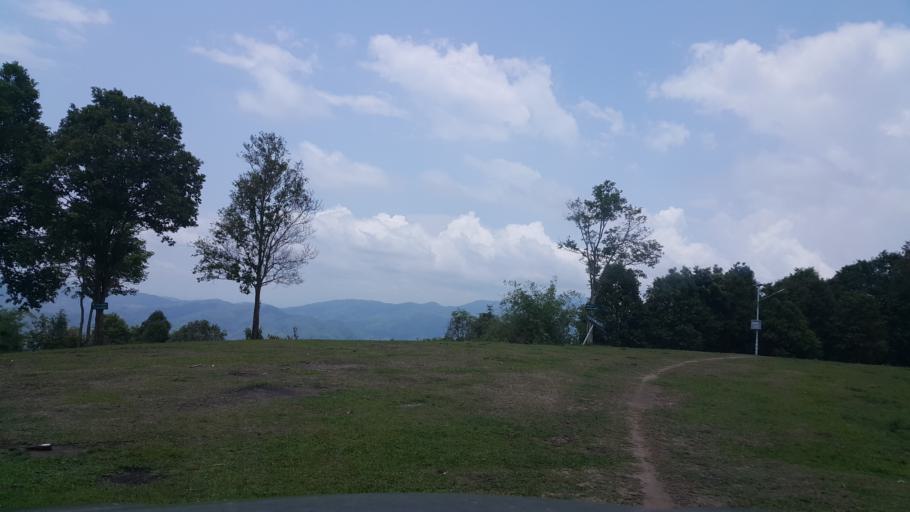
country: TH
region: Chiang Rai
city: Chiang Rai
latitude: 19.9997
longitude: 99.7002
